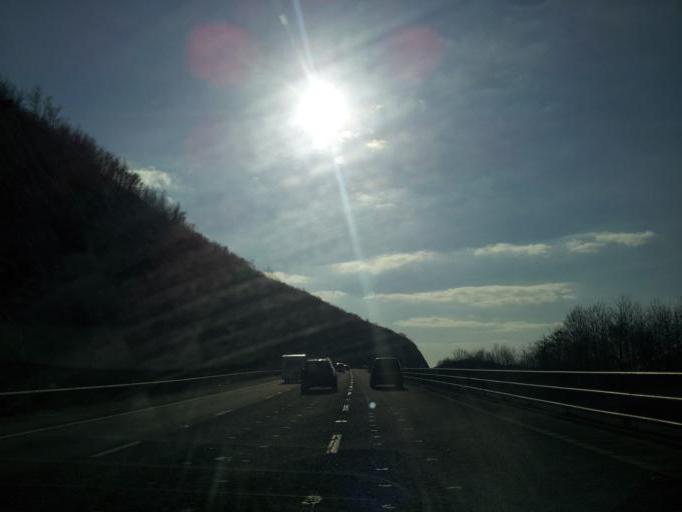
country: GB
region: England
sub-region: North Somerset
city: Portishead
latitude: 51.4507
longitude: -2.7971
